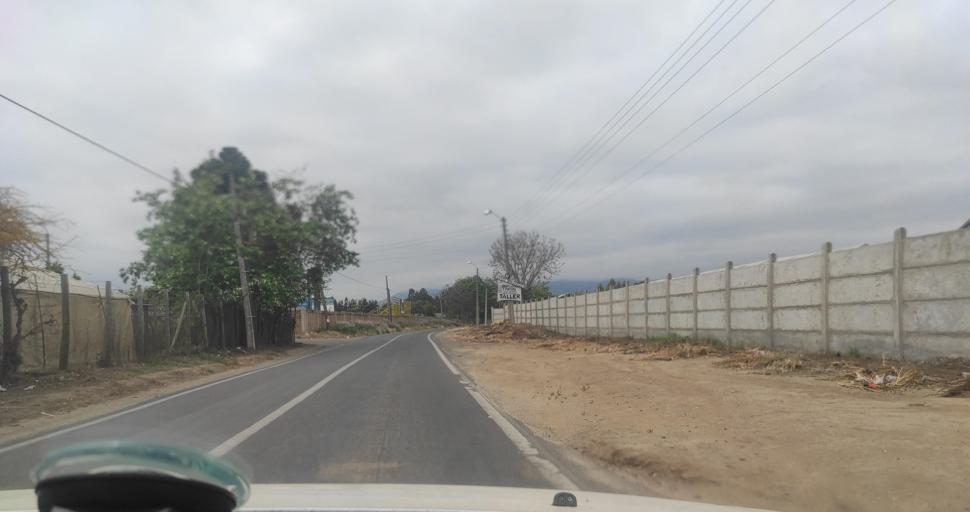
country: CL
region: Valparaiso
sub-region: Provincia de Marga Marga
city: Limache
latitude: -33.0145
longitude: -71.2414
